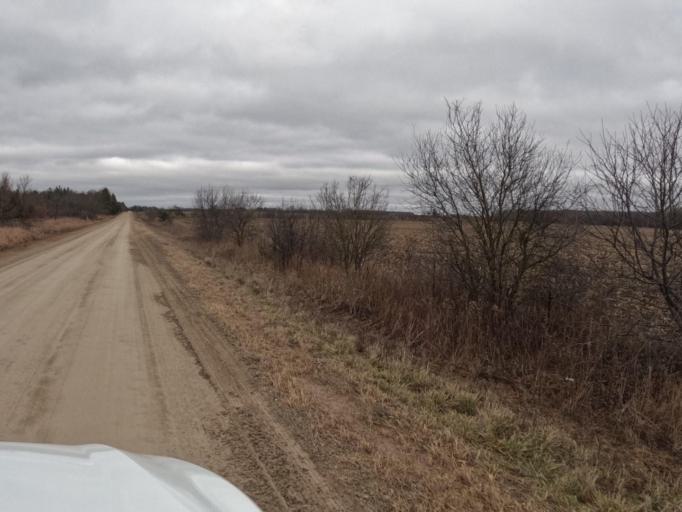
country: CA
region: Ontario
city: Shelburne
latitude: 43.9435
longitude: -80.3954
